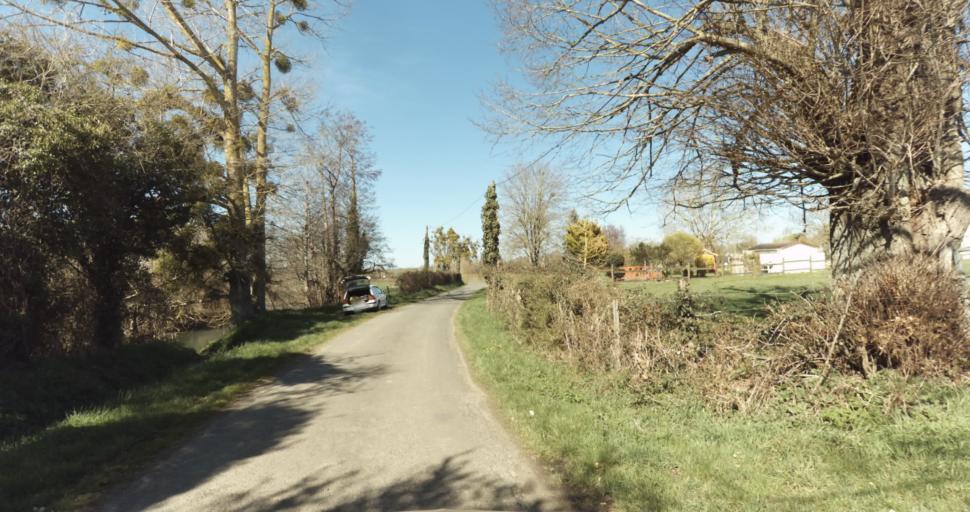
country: FR
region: Lower Normandy
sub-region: Departement du Calvados
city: Saint-Pierre-sur-Dives
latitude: 49.0595
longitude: -0.0262
